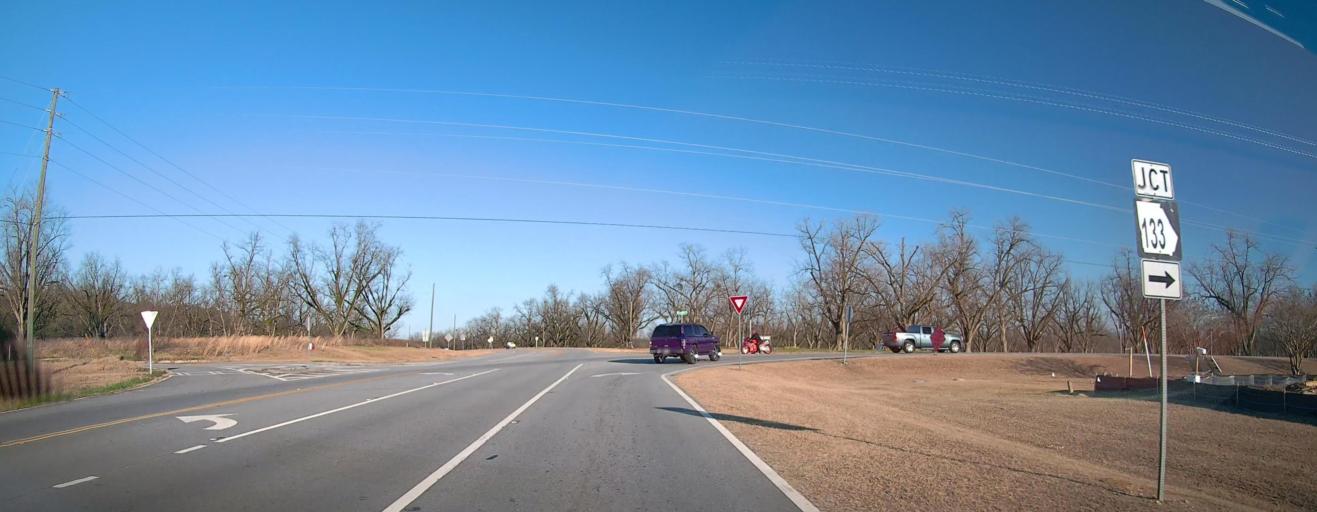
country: US
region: Georgia
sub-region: Lee County
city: Leesburg
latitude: 31.6567
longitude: -84.1717
